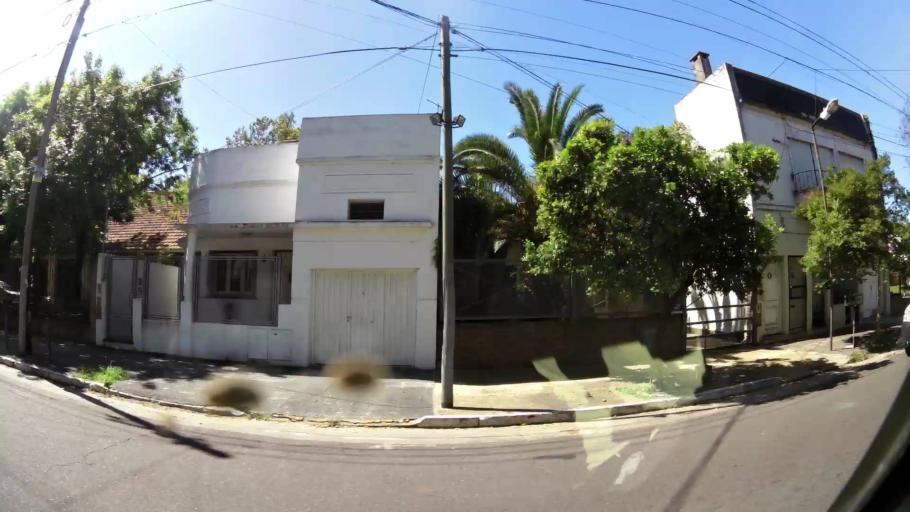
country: AR
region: Buenos Aires
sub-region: Partido de Quilmes
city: Quilmes
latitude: -34.7144
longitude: -58.2893
